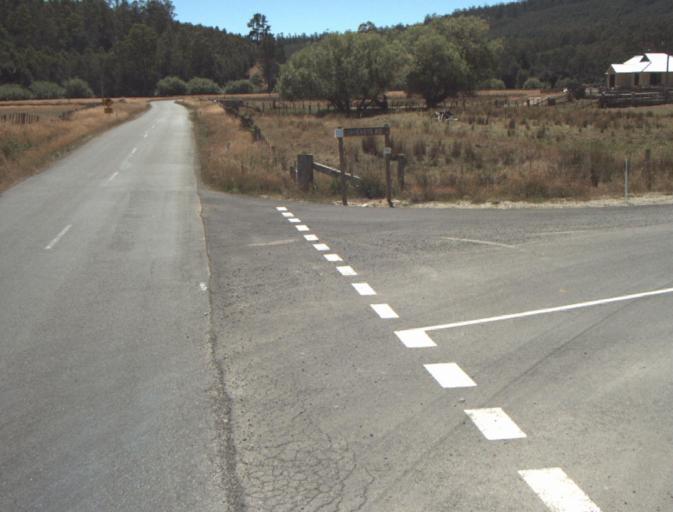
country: AU
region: Tasmania
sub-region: Dorset
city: Scottsdale
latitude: -41.2867
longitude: 147.3840
